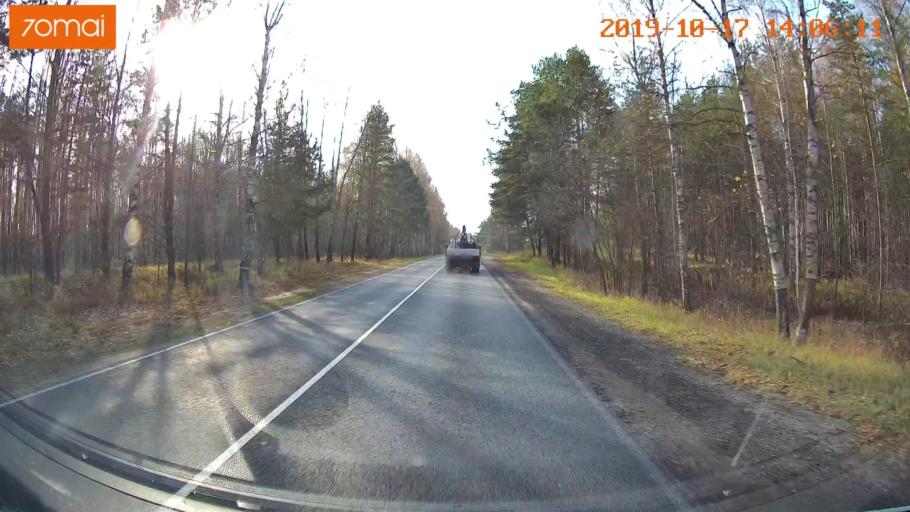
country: RU
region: Rjazan
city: Spas-Klepiki
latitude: 55.1142
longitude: 40.1109
